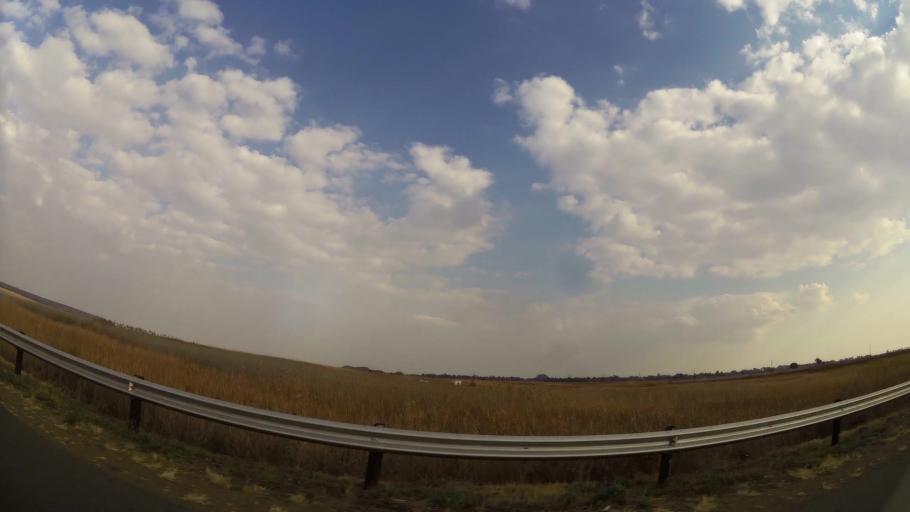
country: ZA
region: Gauteng
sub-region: Ekurhuleni Metropolitan Municipality
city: Springs
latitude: -26.2706
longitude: 28.5005
